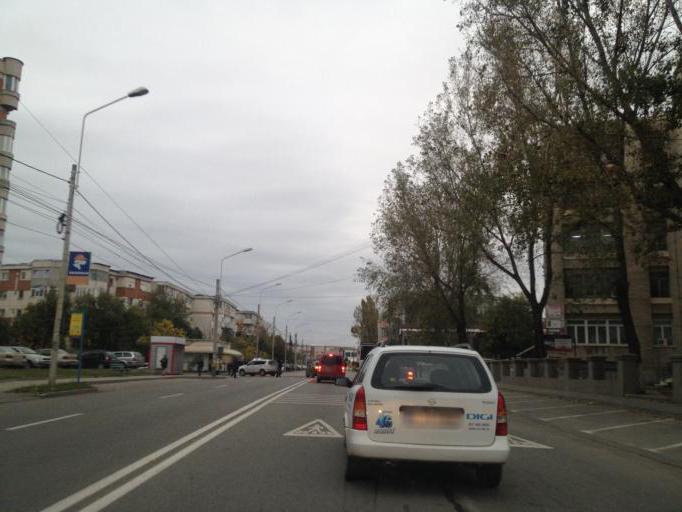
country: RO
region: Dolj
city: Craiova
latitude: 44.3154
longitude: 23.8343
